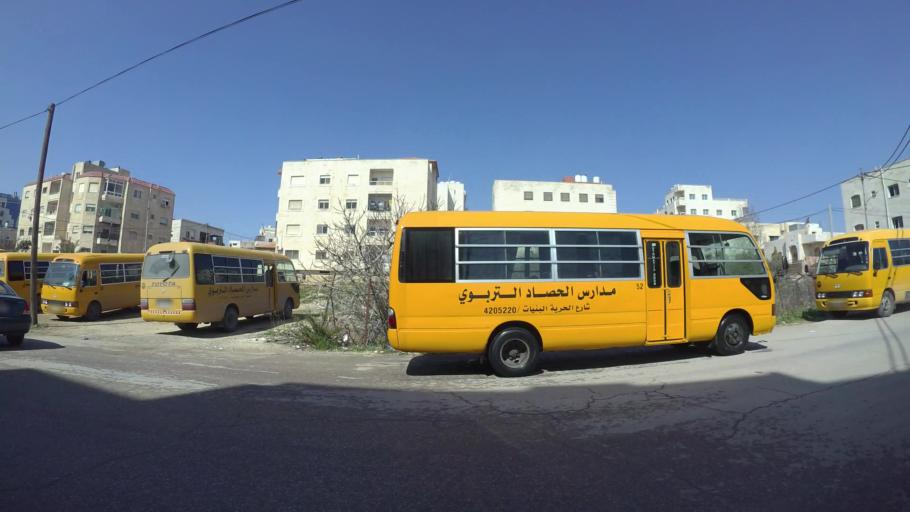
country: JO
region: Amman
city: Al Bunayyat ash Shamaliyah
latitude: 31.8916
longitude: 35.8965
